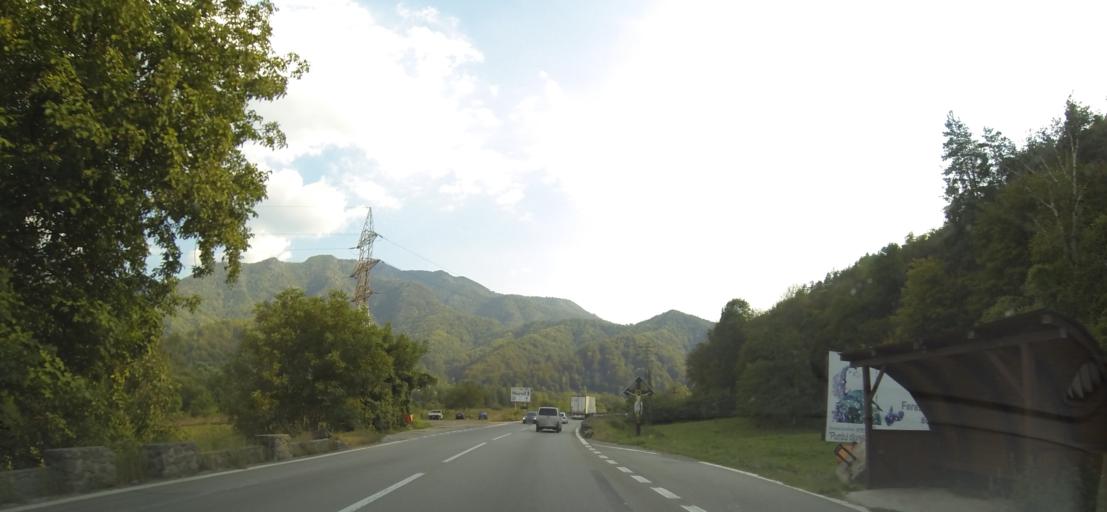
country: RO
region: Valcea
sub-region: Comuna Brezoi
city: Brezoi
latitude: 45.3573
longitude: 24.2967
